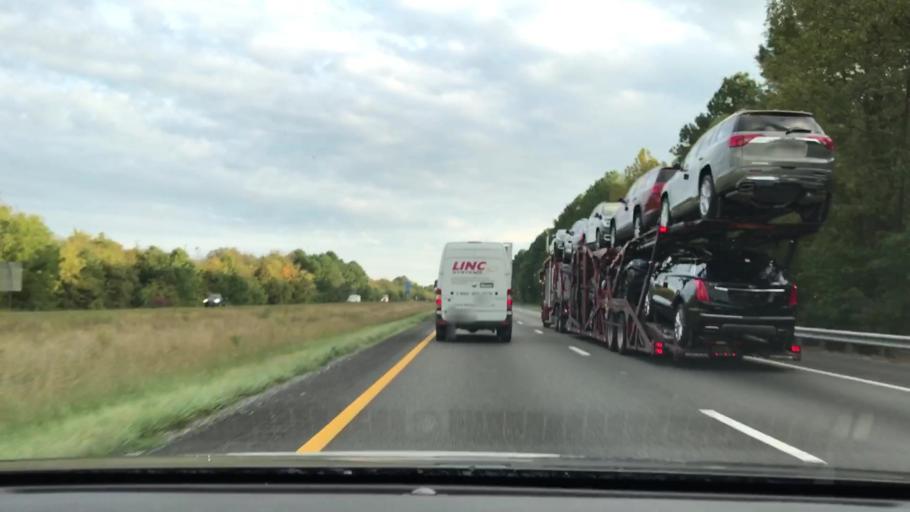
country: US
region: Tennessee
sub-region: Sumner County
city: White House
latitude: 36.4906
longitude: -86.6721
